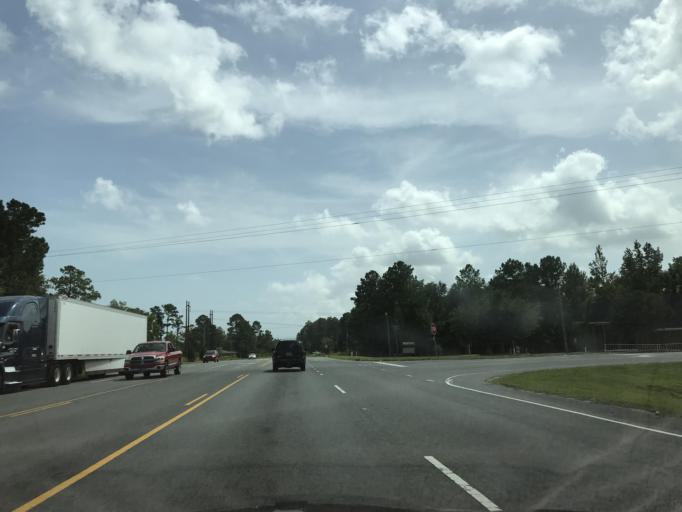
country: US
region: North Carolina
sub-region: New Hanover County
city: Wrightsboro
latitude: 34.3137
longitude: -77.9223
